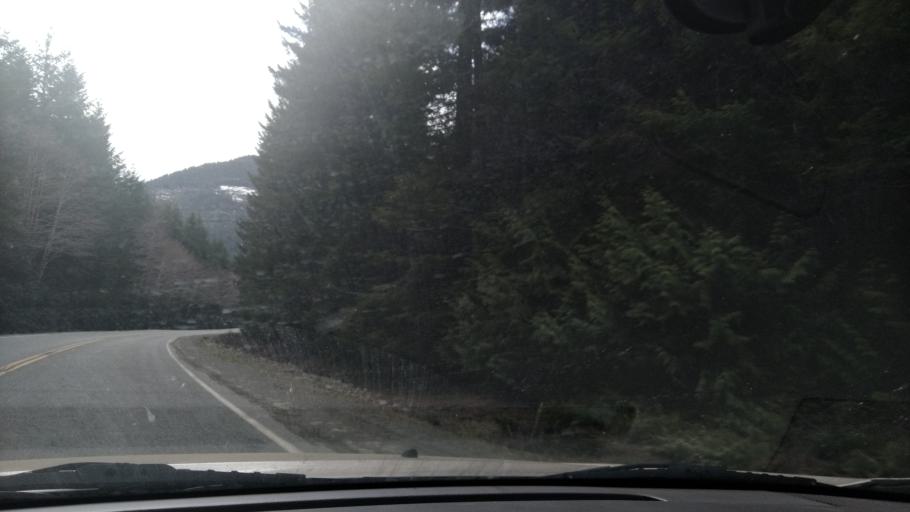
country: CA
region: British Columbia
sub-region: Regional District of Alberni-Clayoquot
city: Tofino
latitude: 49.8323
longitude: -125.9675
